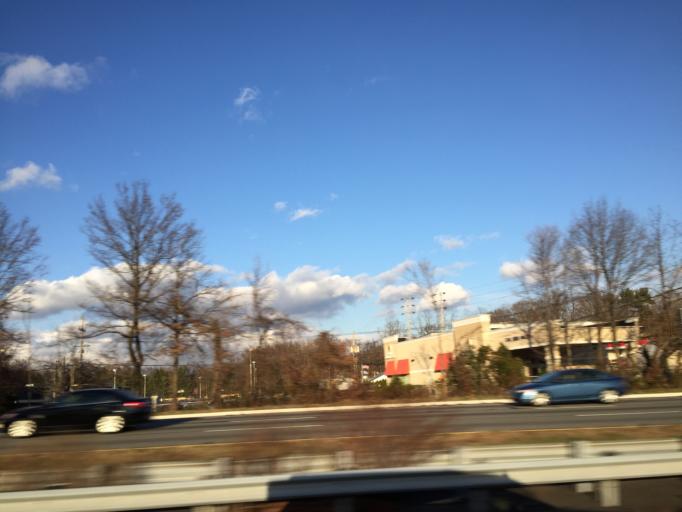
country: US
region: New Jersey
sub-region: Union County
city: Springfield
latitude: 40.7206
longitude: -74.3350
